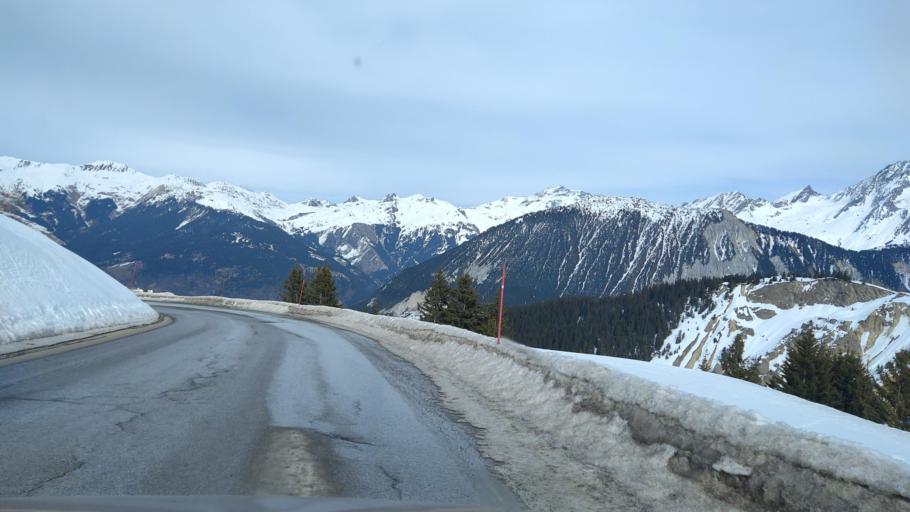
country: FR
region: Rhone-Alpes
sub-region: Departement de la Savoie
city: Courchevel
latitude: 45.3974
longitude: 6.6376
